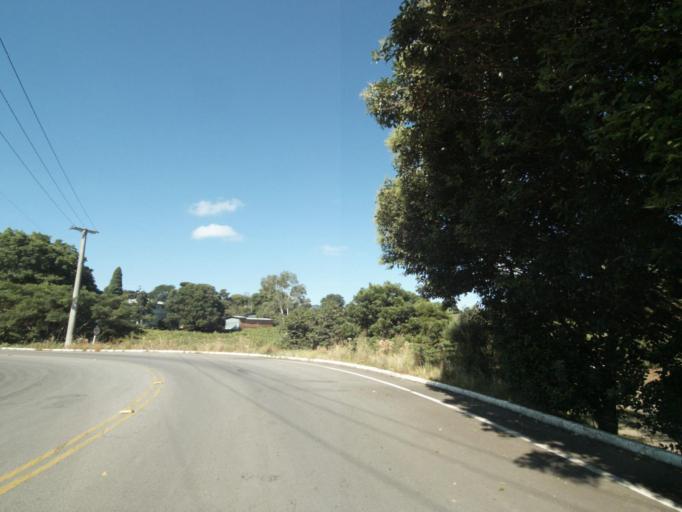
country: BR
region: Rio Grande do Sul
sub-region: Bento Goncalves
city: Bento Goncalves
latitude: -29.1200
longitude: -51.5431
